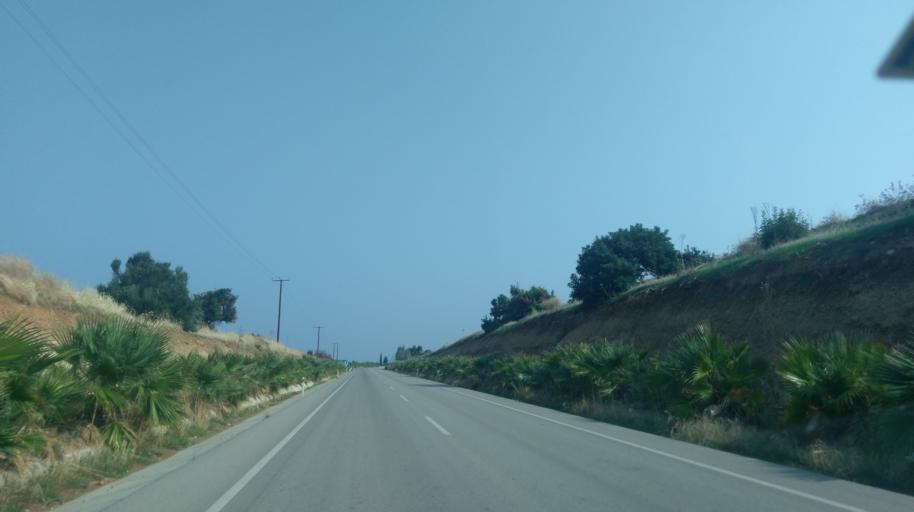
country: CY
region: Ammochostos
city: Trikomo
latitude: 35.4359
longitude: 33.9455
